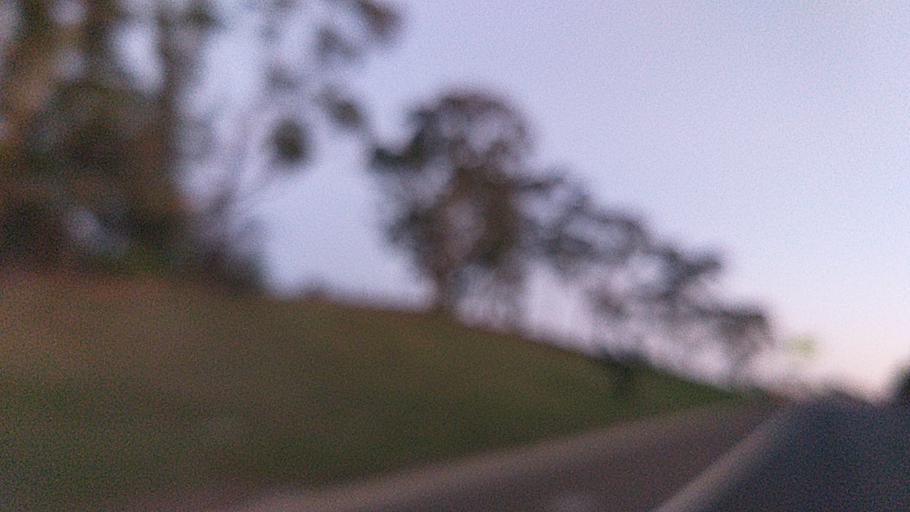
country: AU
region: New South Wales
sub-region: Campbelltown Municipality
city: Leumeah
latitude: -34.0362
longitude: 150.8251
